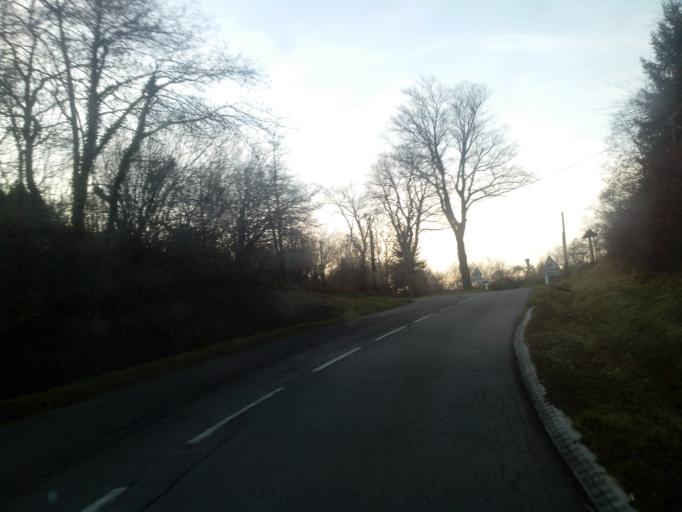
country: FR
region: Languedoc-Roussillon
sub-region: Departement de l'Aude
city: Chalabre
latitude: 42.9092
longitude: 2.0198
